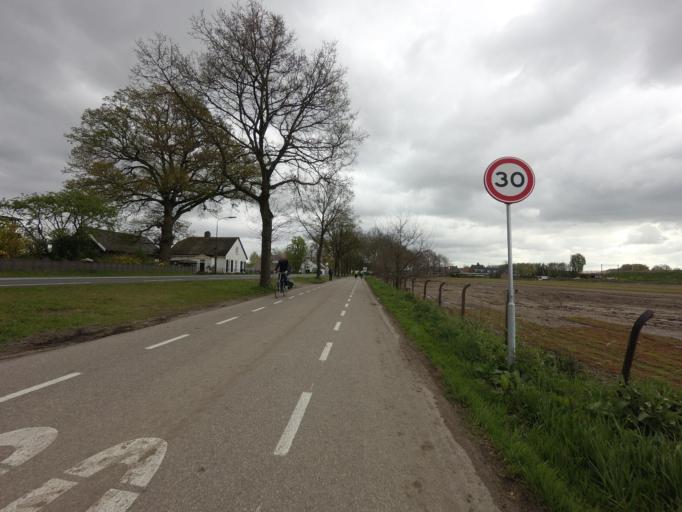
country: NL
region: Utrecht
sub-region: Gemeente Bunnik
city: Bunnik
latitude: 52.0640
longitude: 5.1695
